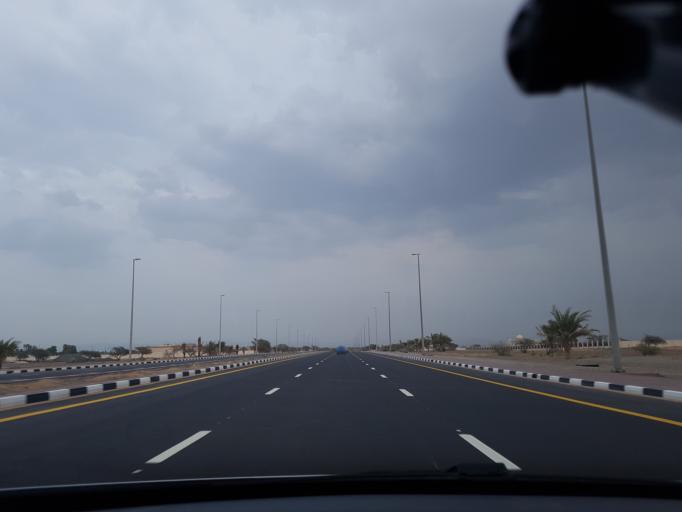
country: AE
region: Ash Shariqah
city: Adh Dhayd
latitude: 25.2675
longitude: 55.9048
